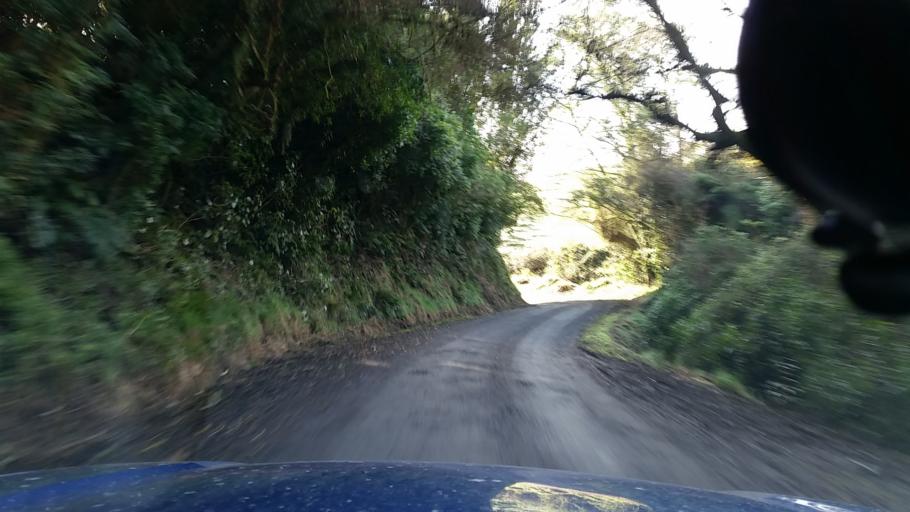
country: NZ
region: Taranaki
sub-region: New Plymouth District
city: Waitara
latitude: -39.0619
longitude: 174.7893
